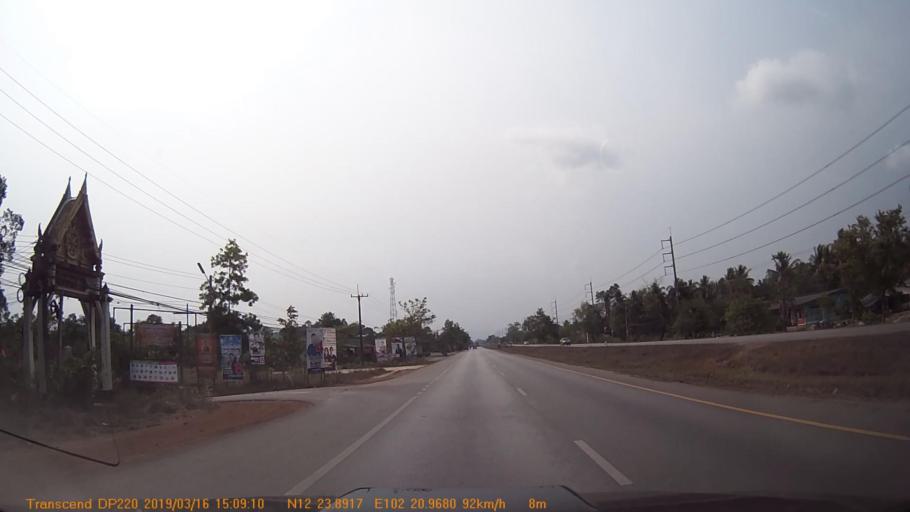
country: TH
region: Trat
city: Khao Saming
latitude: 12.3984
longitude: 102.3492
